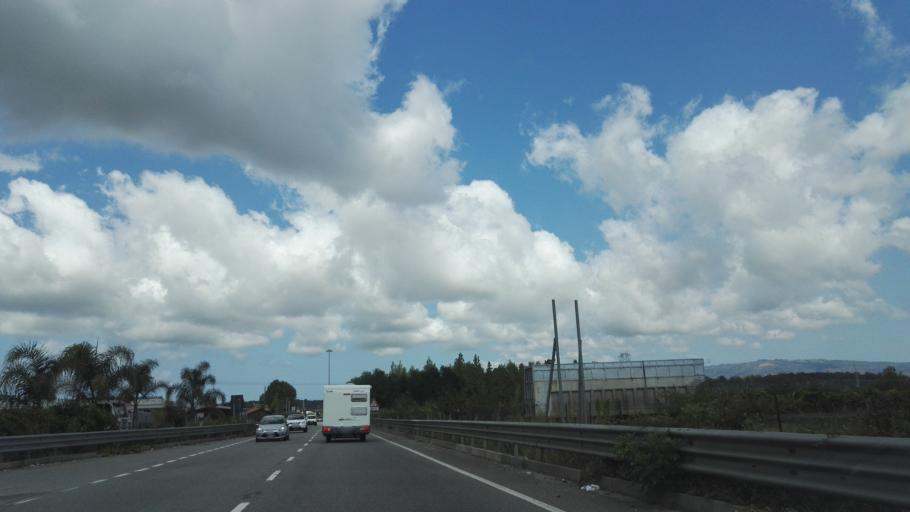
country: IT
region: Calabria
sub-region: Provincia di Reggio Calabria
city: Rosarno
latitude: 38.4646
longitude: 16.0126
